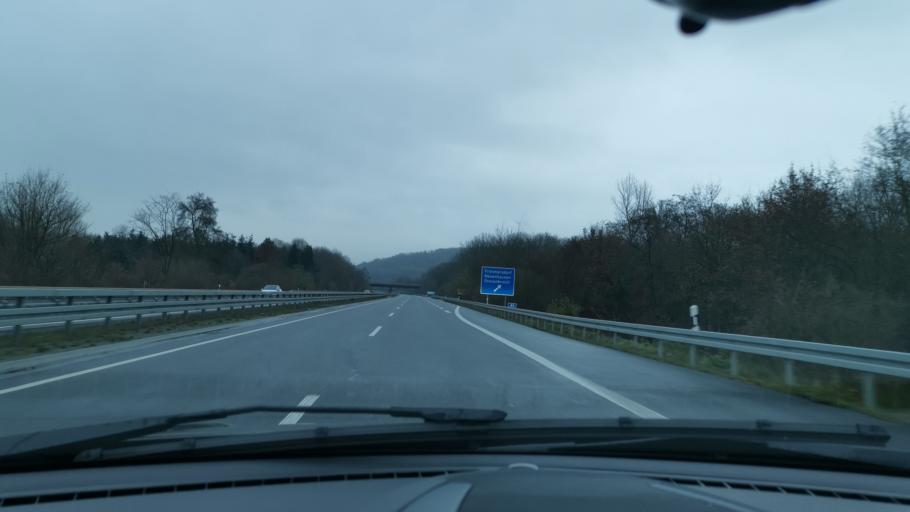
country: DE
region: North Rhine-Westphalia
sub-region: Regierungsbezirk Dusseldorf
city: Grevenbroich
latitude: 51.0776
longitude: 6.5847
